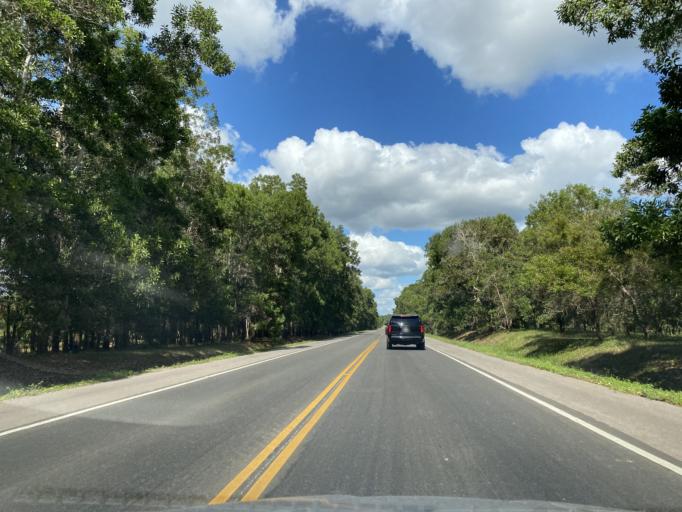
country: DO
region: Monte Plata
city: Monte Plata
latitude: 18.7515
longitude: -69.7659
